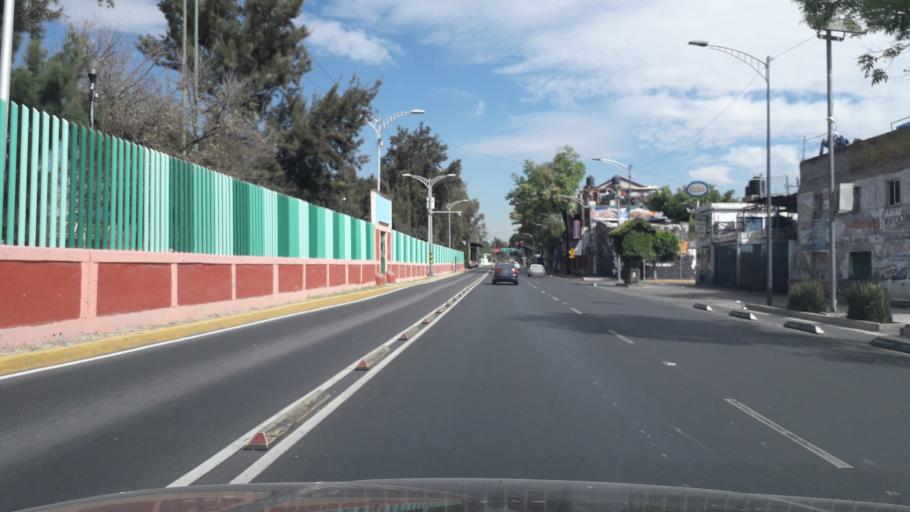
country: MX
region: Mexico City
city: Gustavo A. Madero
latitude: 19.4993
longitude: -99.0889
